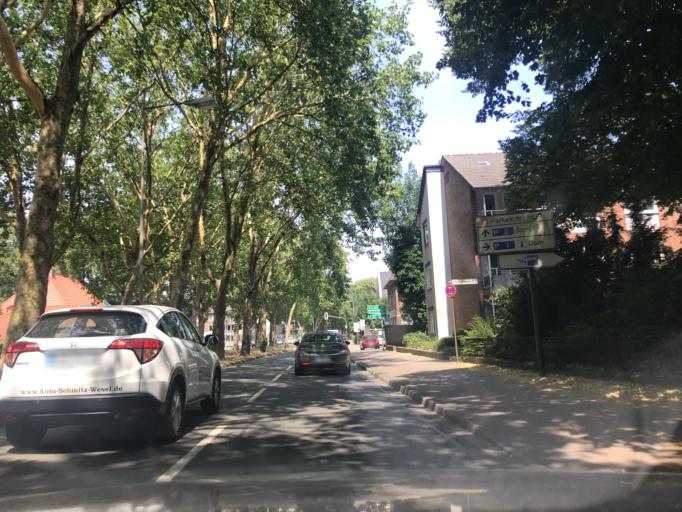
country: DE
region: North Rhine-Westphalia
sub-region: Regierungsbezirk Dusseldorf
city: Wesel
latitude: 51.6553
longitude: 6.6082
